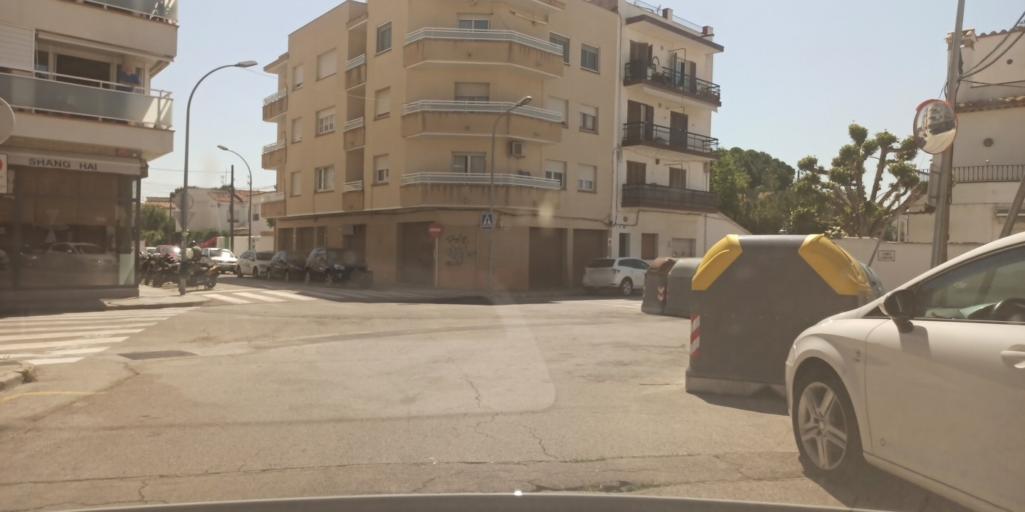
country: ES
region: Catalonia
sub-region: Provincia de Barcelona
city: Sant Pere de Ribes
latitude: 41.2577
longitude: 1.7712
